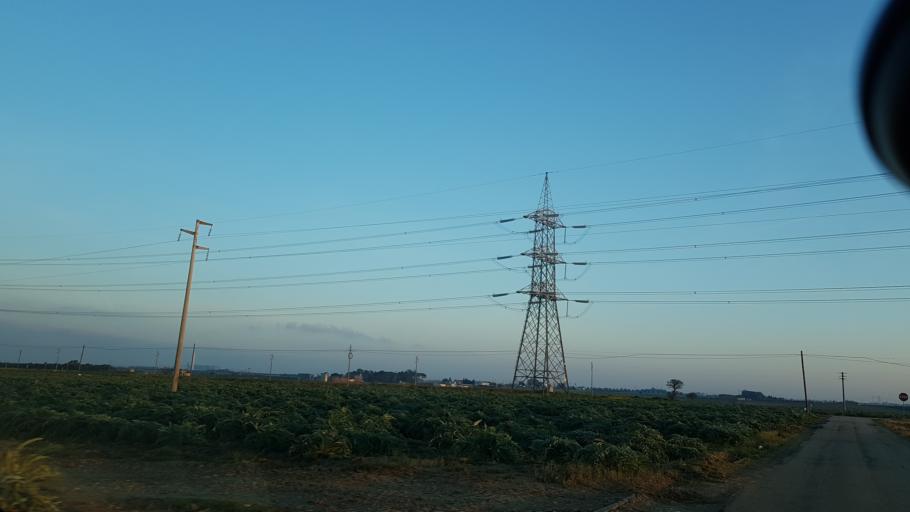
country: IT
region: Apulia
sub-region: Provincia di Brindisi
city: La Rosa
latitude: 40.5936
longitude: 17.9517
